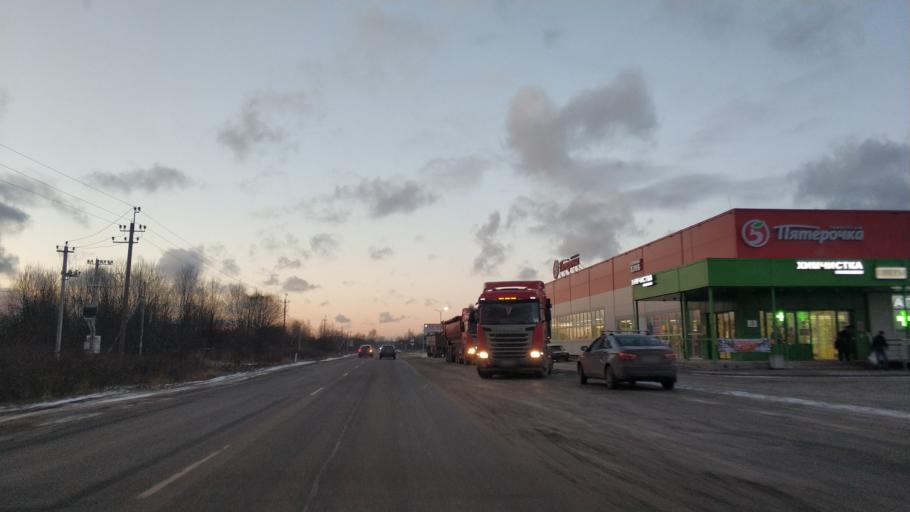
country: RU
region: St.-Petersburg
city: Pontonnyy
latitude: 59.8017
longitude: 30.6331
